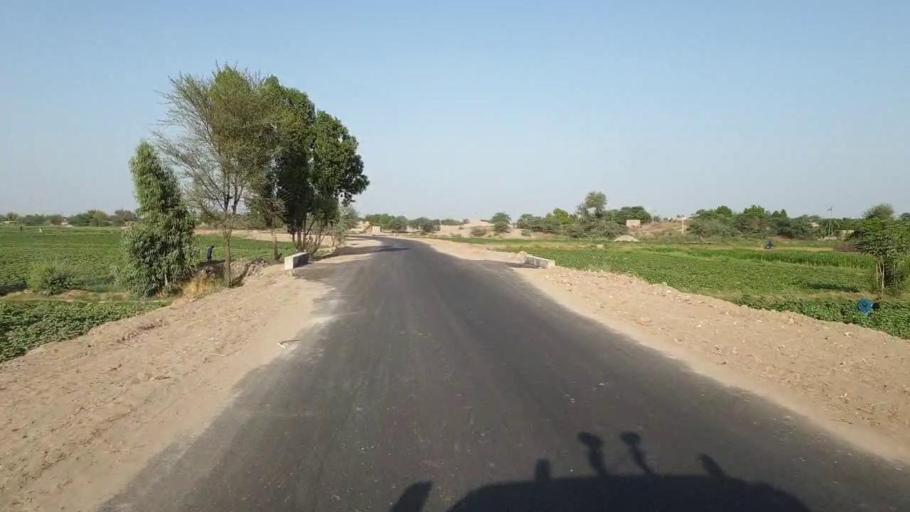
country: PK
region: Sindh
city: Jam Sahib
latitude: 26.3475
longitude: 68.5579
